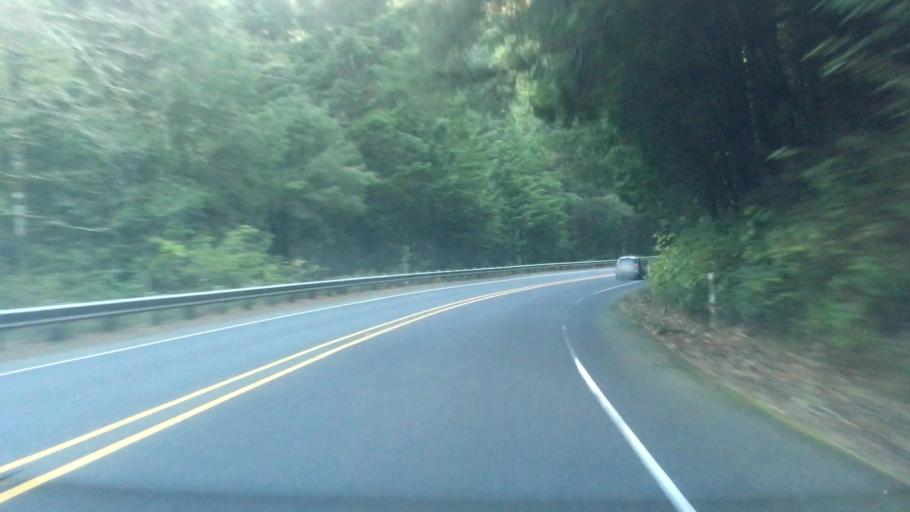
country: US
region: Oregon
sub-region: Clatsop County
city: Cannon Beach
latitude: 45.7735
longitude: -123.9436
